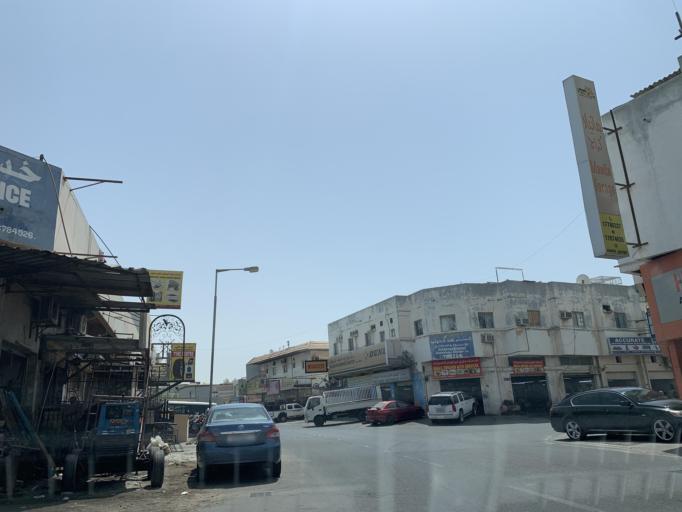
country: BH
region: Northern
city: Madinat `Isa
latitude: 26.1926
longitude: 50.5401
